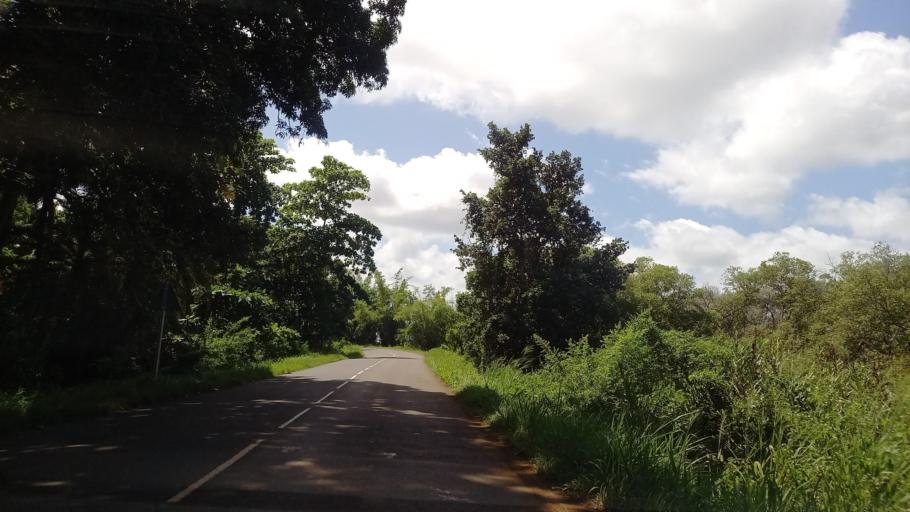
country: YT
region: Bandraboua
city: Bandraboua
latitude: -12.7224
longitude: 45.1291
